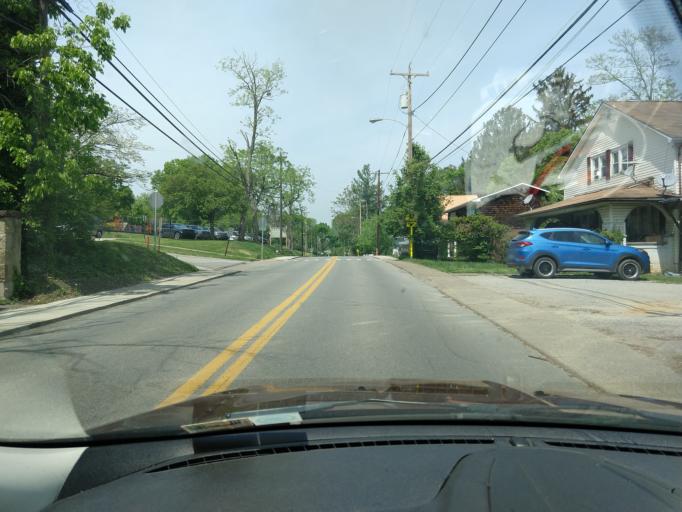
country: US
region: West Virginia
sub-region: Kanawha County
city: Saint Albans
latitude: 38.3831
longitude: -81.8303
